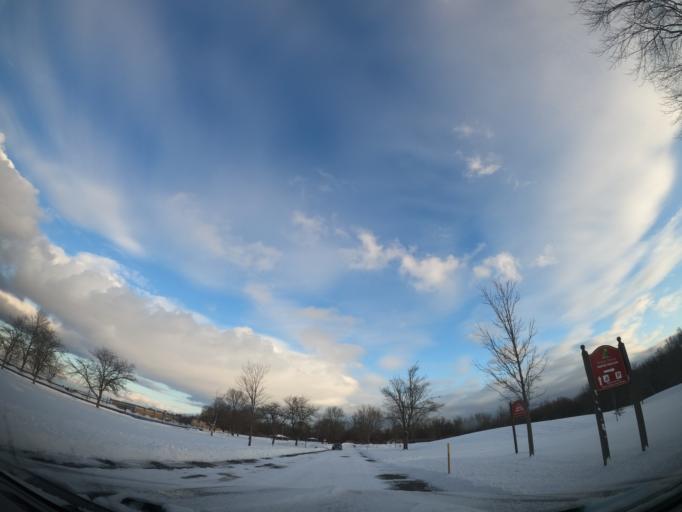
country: US
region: New York
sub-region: Onondaga County
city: Brewerton
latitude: 43.2246
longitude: -76.1095
